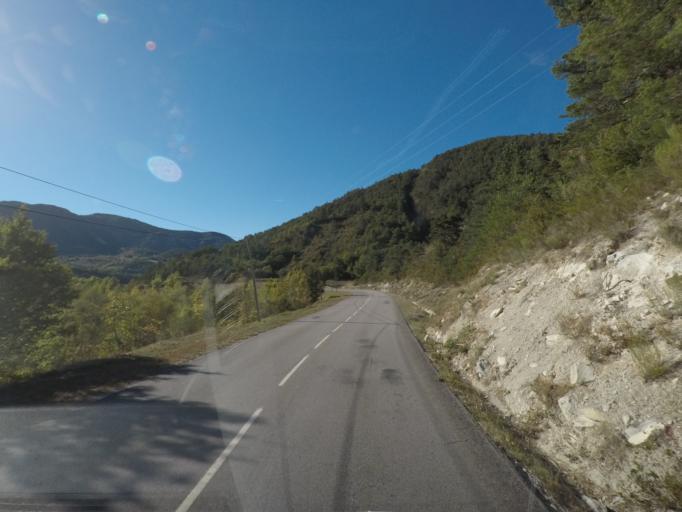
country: FR
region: Rhone-Alpes
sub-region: Departement de la Drome
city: Buis-les-Baronnies
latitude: 44.4662
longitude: 5.4350
